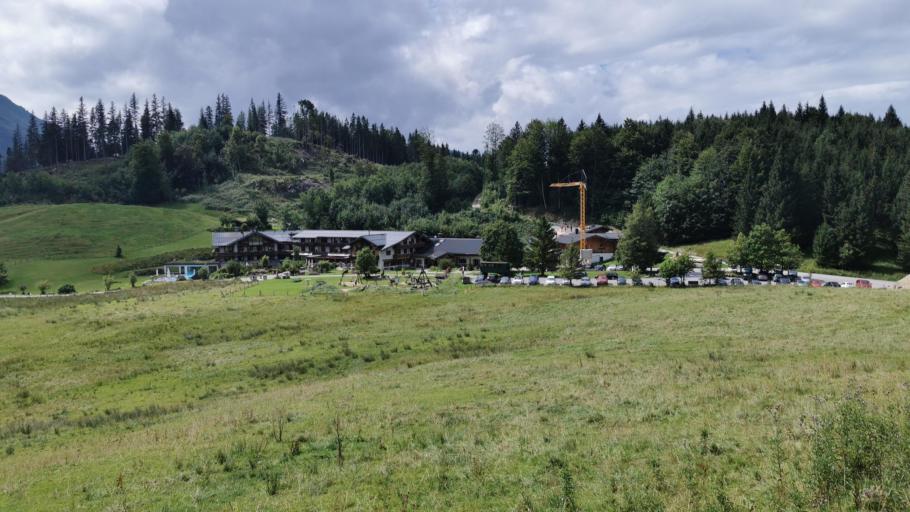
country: DE
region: Bavaria
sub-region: Swabia
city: Pfronten
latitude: 47.5703
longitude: 10.5890
